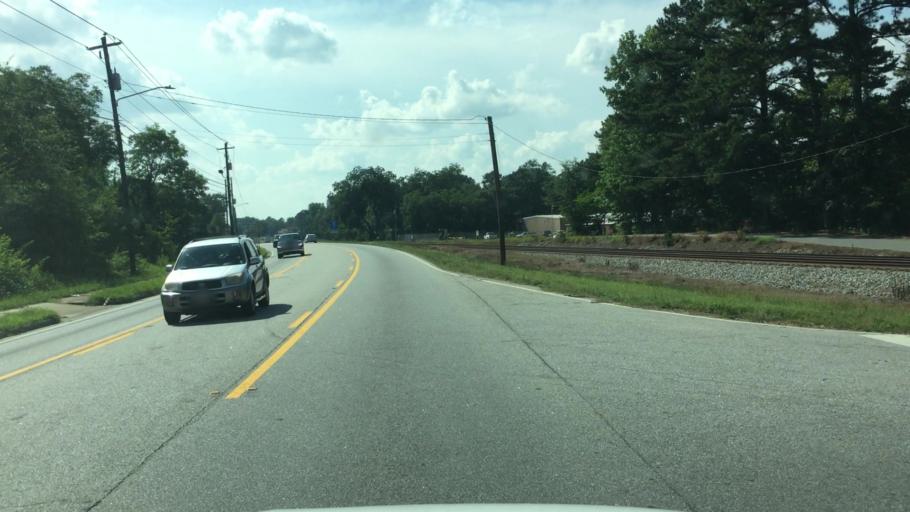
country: US
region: Georgia
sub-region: Barrow County
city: Auburn
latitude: 34.0087
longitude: -83.8166
